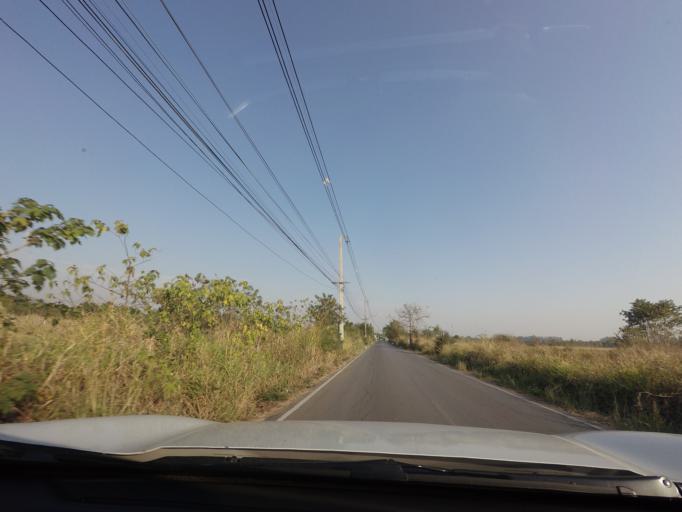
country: TH
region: Nakhon Ratchasima
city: Pak Chong
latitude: 14.5988
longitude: 101.4449
